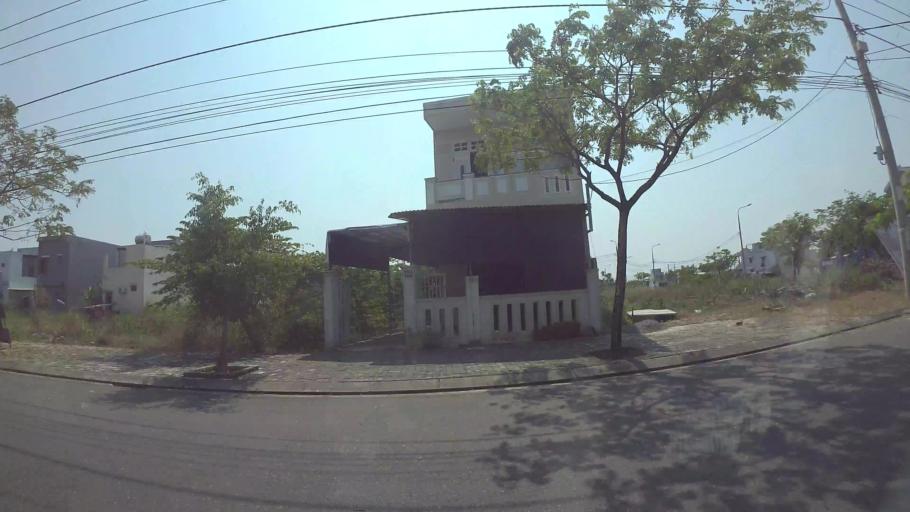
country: VN
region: Da Nang
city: Ngu Hanh Son
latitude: 15.9839
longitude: 108.2717
